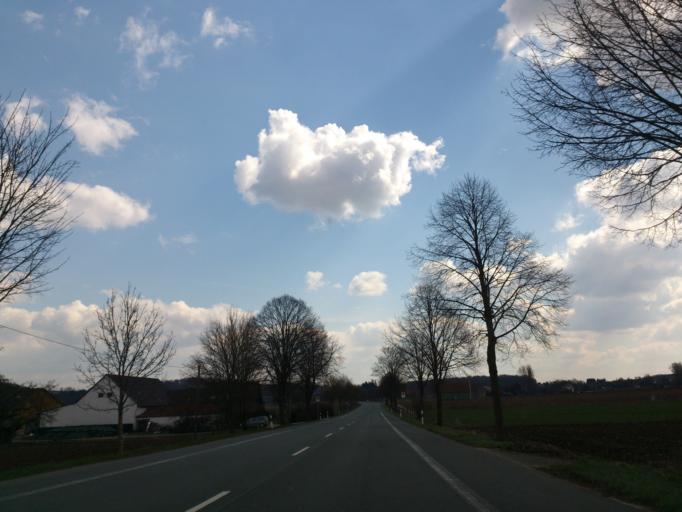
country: DE
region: North Rhine-Westphalia
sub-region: Regierungsbezirk Detmold
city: Willebadessen
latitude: 51.5914
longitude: 9.0352
